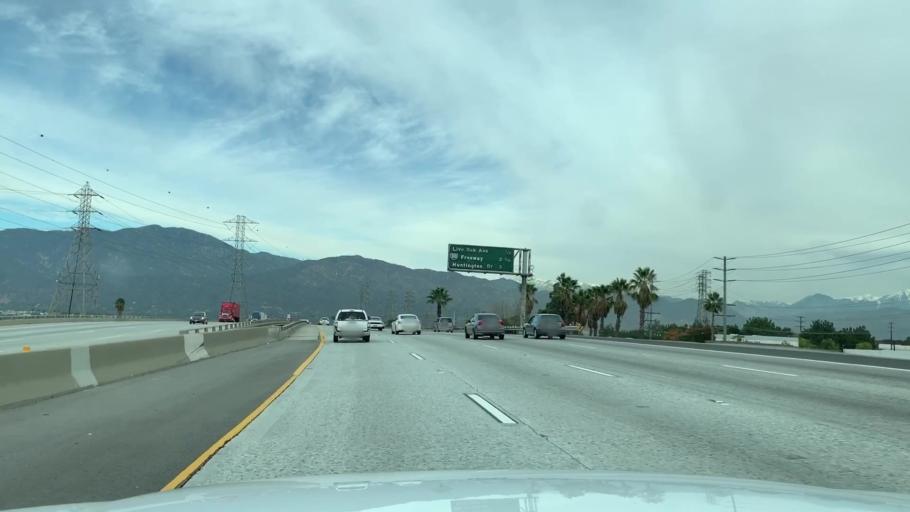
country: US
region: California
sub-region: Los Angeles County
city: Baldwin Park
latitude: 34.0974
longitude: -117.9858
